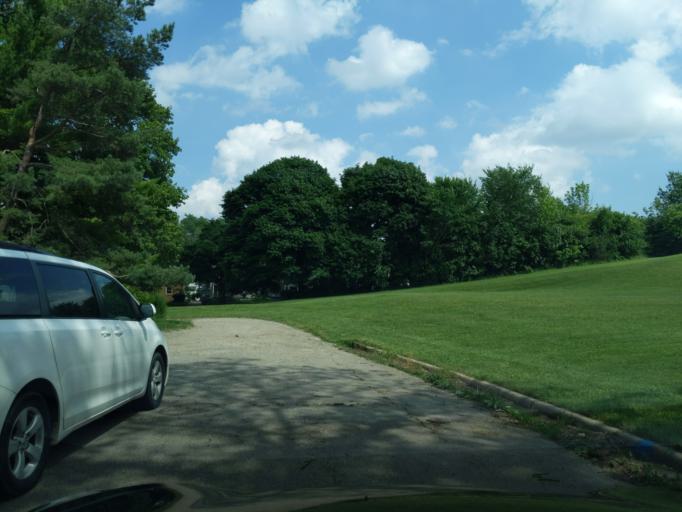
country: US
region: Michigan
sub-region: Ingham County
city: Lansing
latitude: 42.7168
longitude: -84.5734
